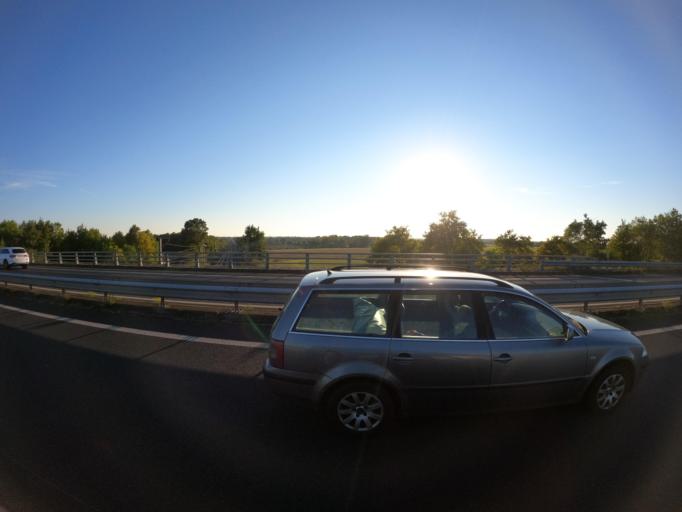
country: FR
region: Pays de la Loire
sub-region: Departement de la Vendee
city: Bouffere
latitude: 46.9368
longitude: -1.3442
